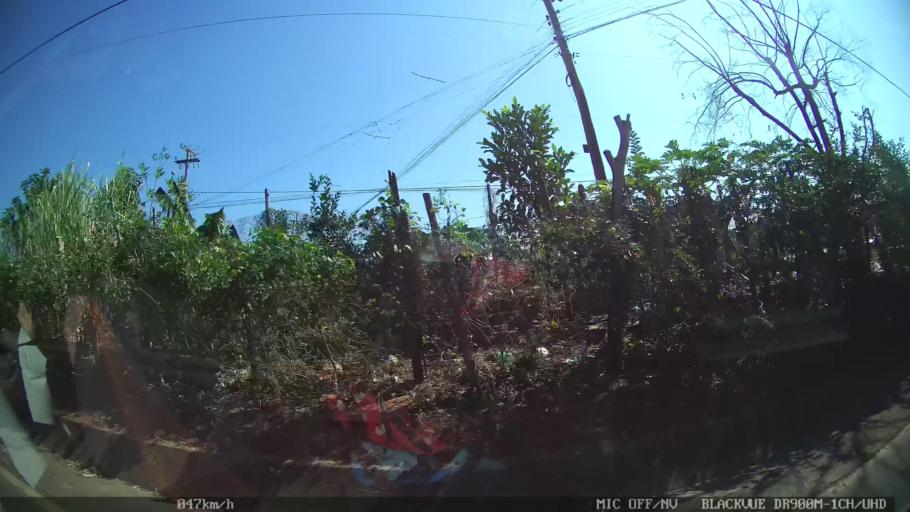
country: BR
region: Sao Paulo
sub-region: Indaiatuba
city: Indaiatuba
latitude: -23.0388
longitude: -47.1093
